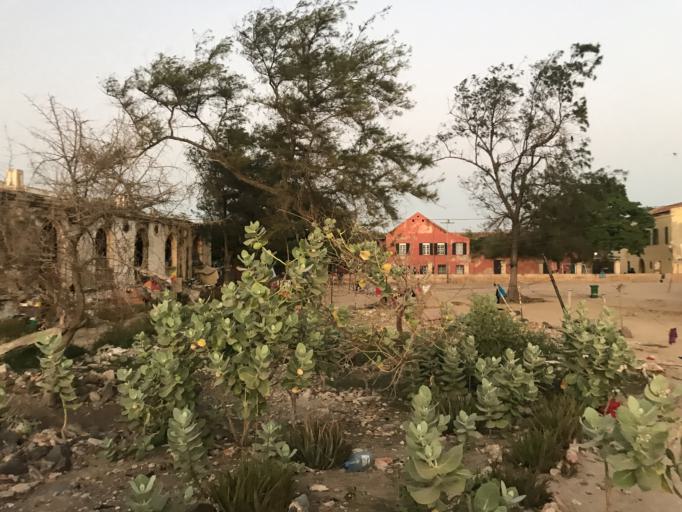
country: SN
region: Dakar
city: Dakar
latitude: 14.6672
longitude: -17.3999
